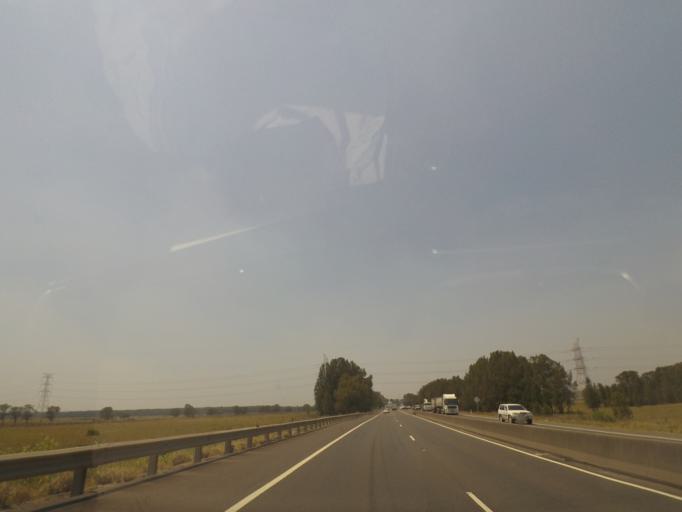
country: AU
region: New South Wales
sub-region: Newcastle
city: Beresfield
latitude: -32.8114
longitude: 151.6750
